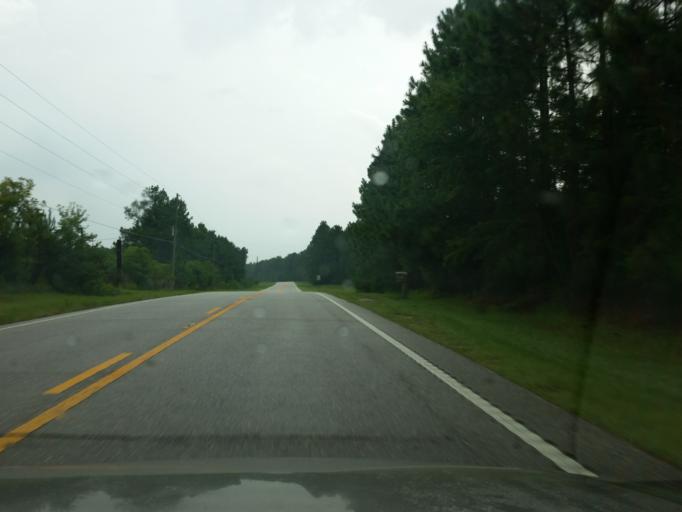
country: US
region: Alabama
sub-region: Baldwin County
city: Elberta
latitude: 30.5232
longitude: -87.4942
